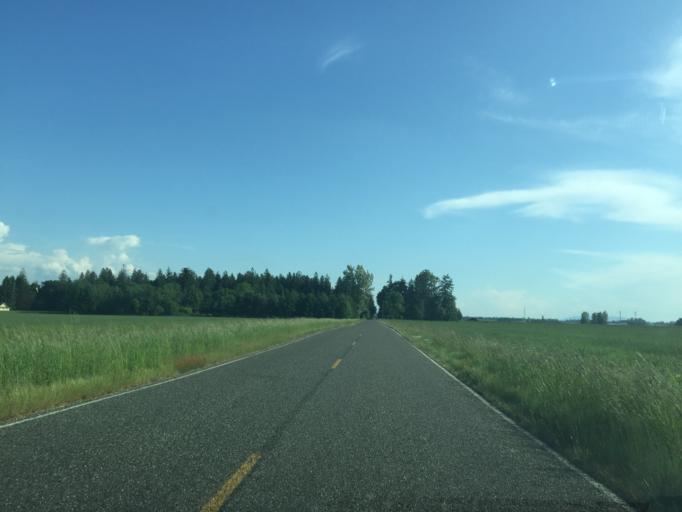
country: US
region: Washington
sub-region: Whatcom County
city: Lynden
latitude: 48.9829
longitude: -122.4627
